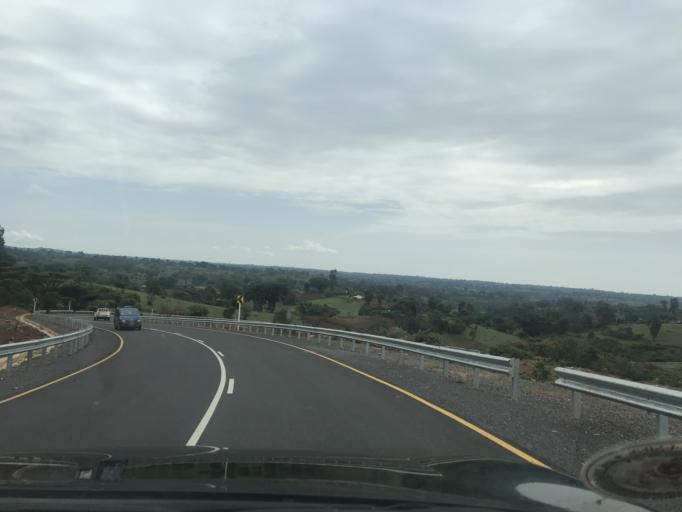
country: ET
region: Oromiya
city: Shambu
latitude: 9.8701
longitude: 36.6934
